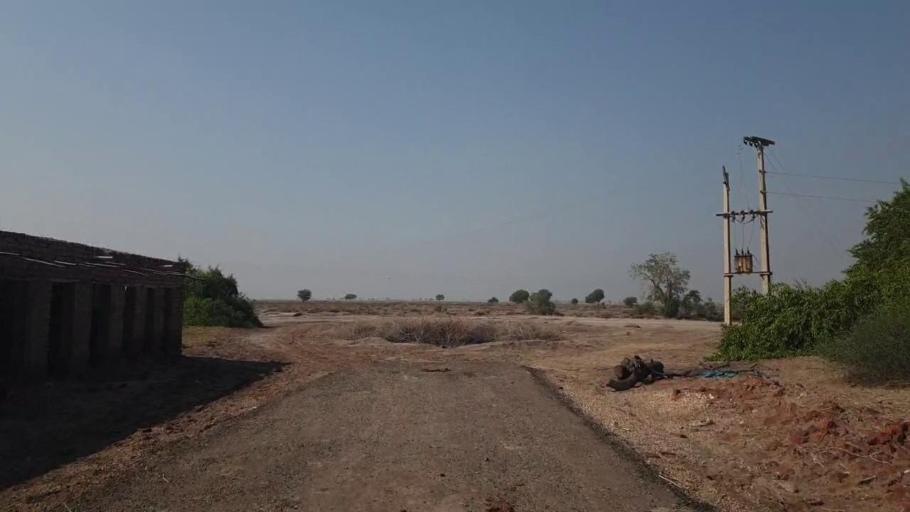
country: PK
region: Sindh
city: Sehwan
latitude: 26.4298
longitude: 67.7560
